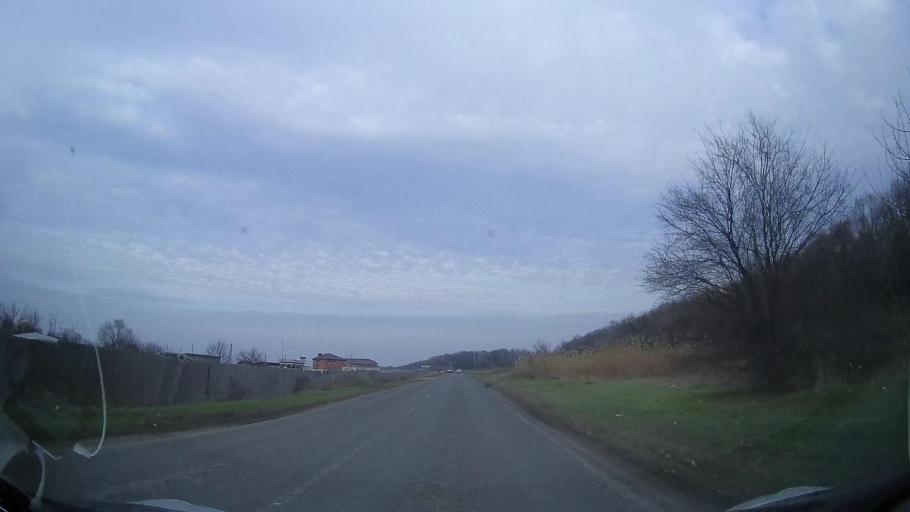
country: RU
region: Rostov
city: Ol'ginskaya
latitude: 47.1339
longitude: 39.8894
